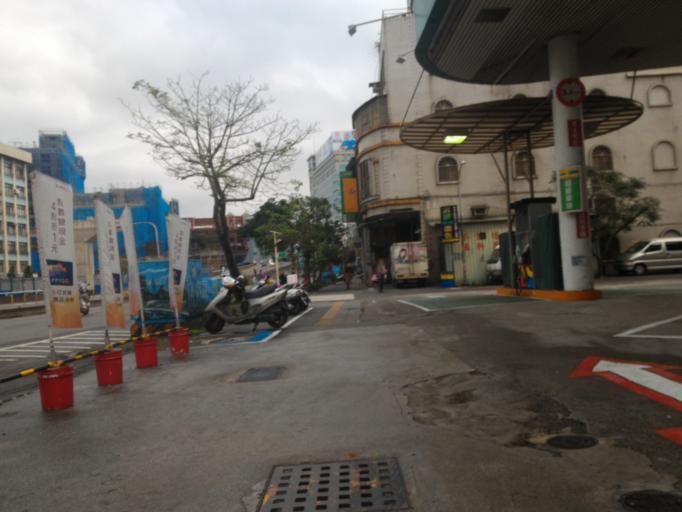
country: TW
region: Taipei
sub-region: Taipei
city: Banqiao
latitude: 25.0416
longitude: 121.4598
